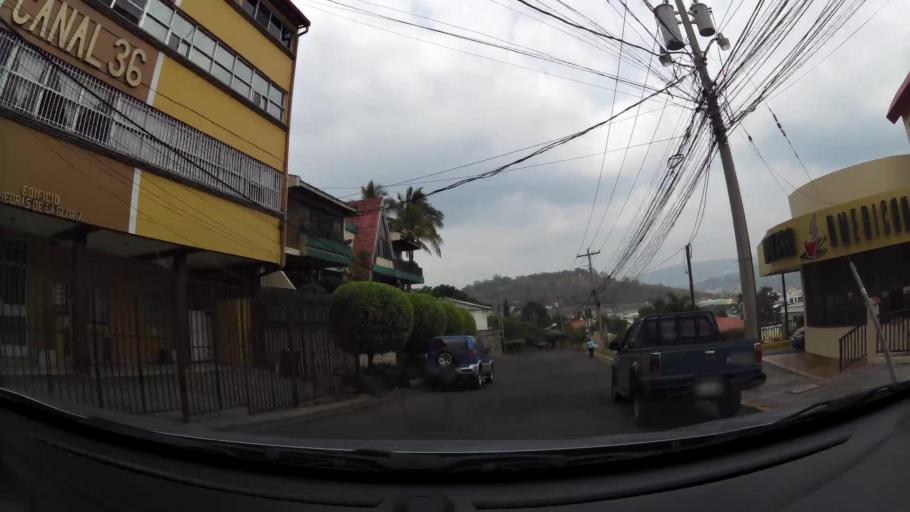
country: HN
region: Francisco Morazan
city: Tegucigalpa
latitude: 14.0947
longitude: -87.1919
